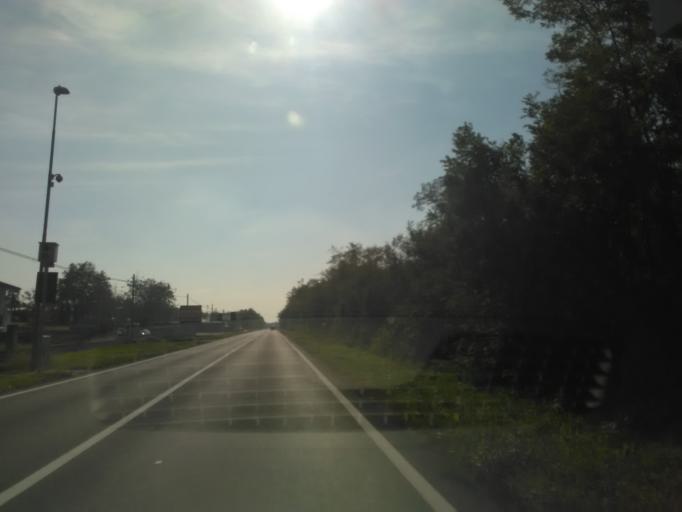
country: IT
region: Piedmont
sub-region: Provincia di Vercelli
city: Lenta
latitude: 45.5742
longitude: 8.3785
